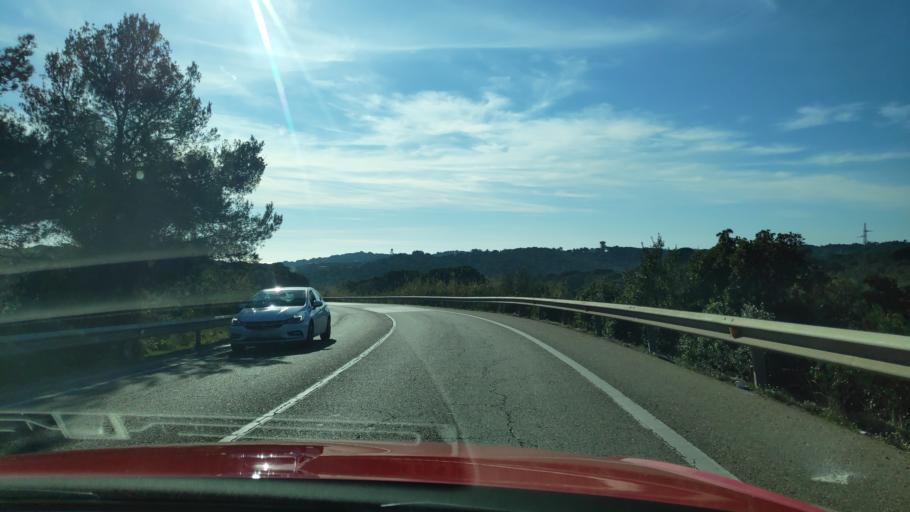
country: ES
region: Catalonia
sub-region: Provincia de Girona
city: Lloret de Mar
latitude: 41.7215
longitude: 2.8250
